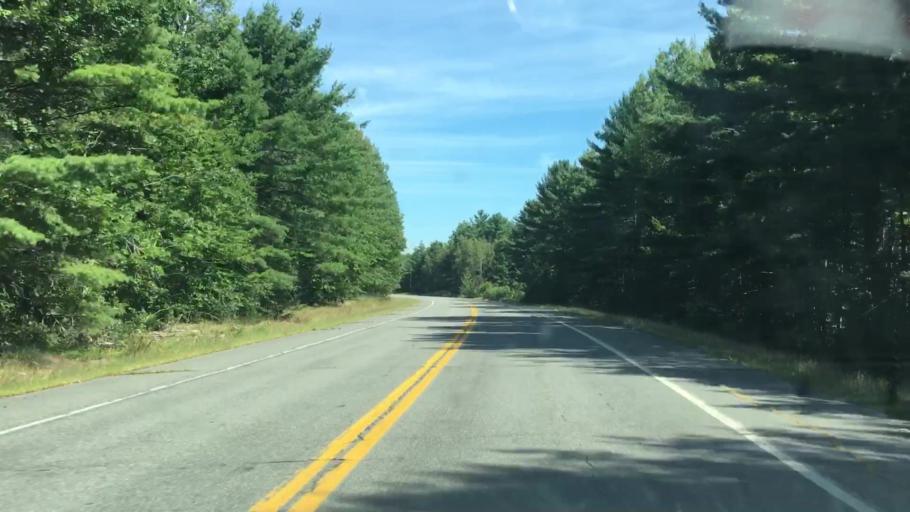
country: US
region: Maine
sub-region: Piscataquis County
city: Milo
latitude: 45.2290
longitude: -68.9474
